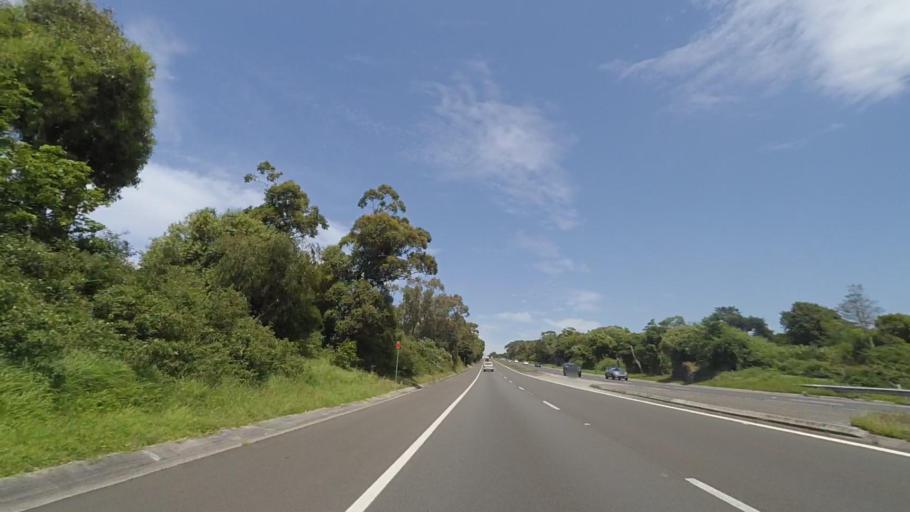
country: AU
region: New South Wales
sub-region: Kiama
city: Kiama
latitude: -34.6680
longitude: 150.8450
